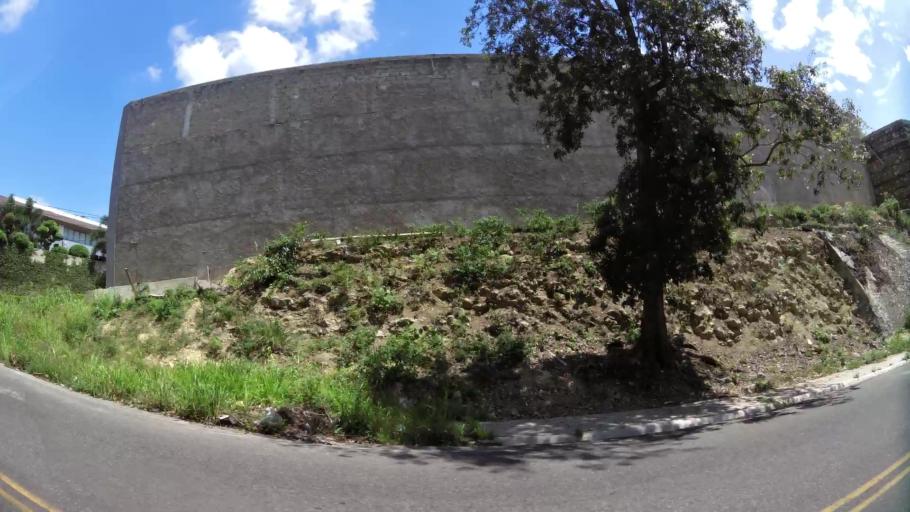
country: DO
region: Santiago
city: Santiago de los Caballeros
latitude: 19.4659
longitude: -70.6804
